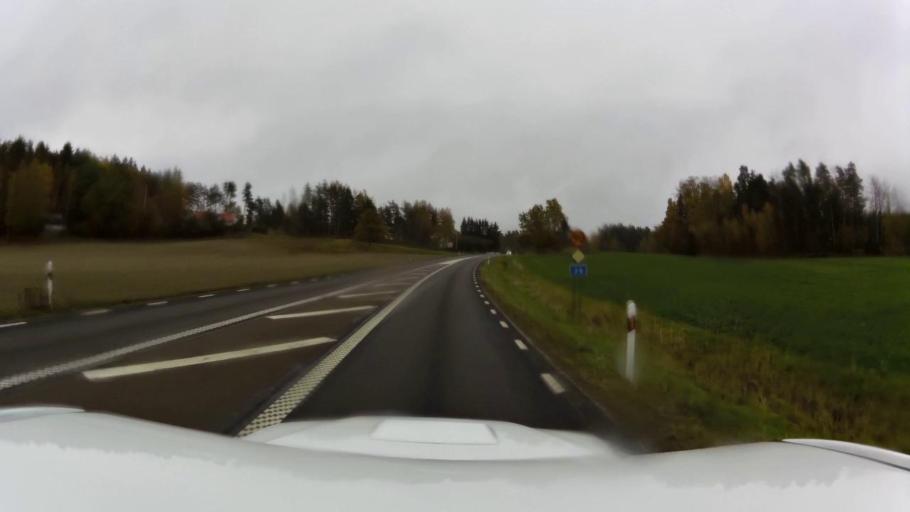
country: SE
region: OEstergoetland
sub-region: Linkopings Kommun
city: Linghem
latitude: 58.3710
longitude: 15.8163
